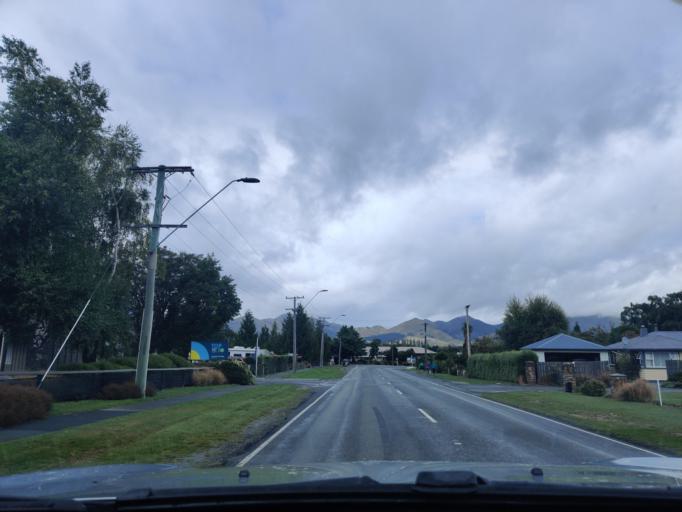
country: NZ
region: Canterbury
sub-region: Hurunui District
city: Amberley
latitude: -42.5278
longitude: 172.8293
